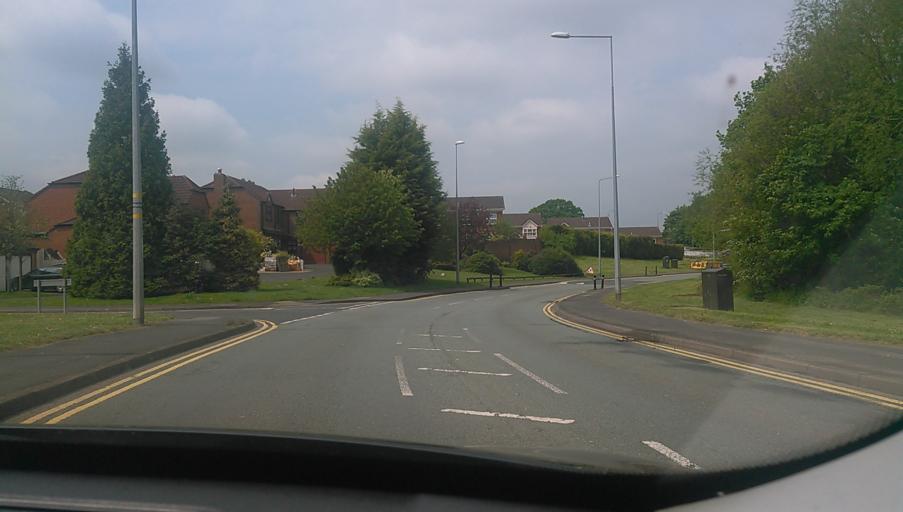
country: GB
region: England
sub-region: Telford and Wrekin
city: Wellington
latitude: 52.7099
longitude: -2.5055
